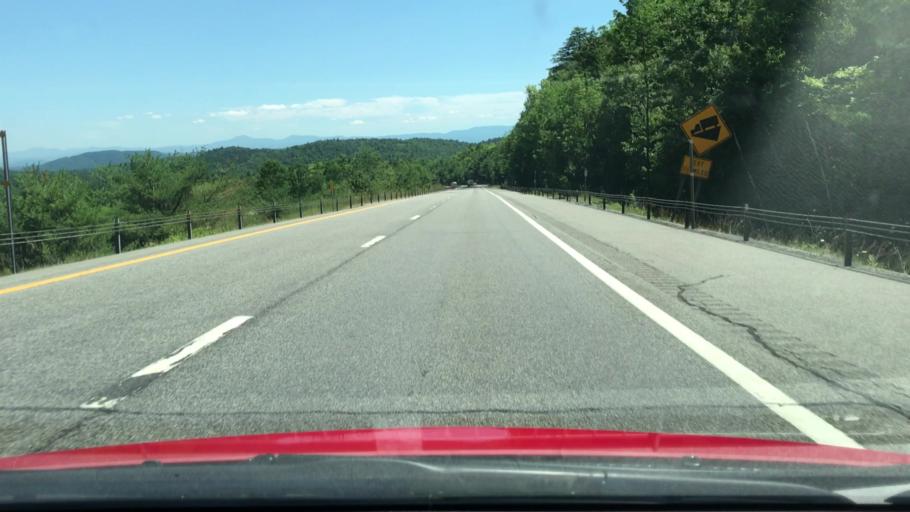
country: US
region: New York
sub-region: Essex County
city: Elizabethtown
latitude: 44.1912
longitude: -73.5527
